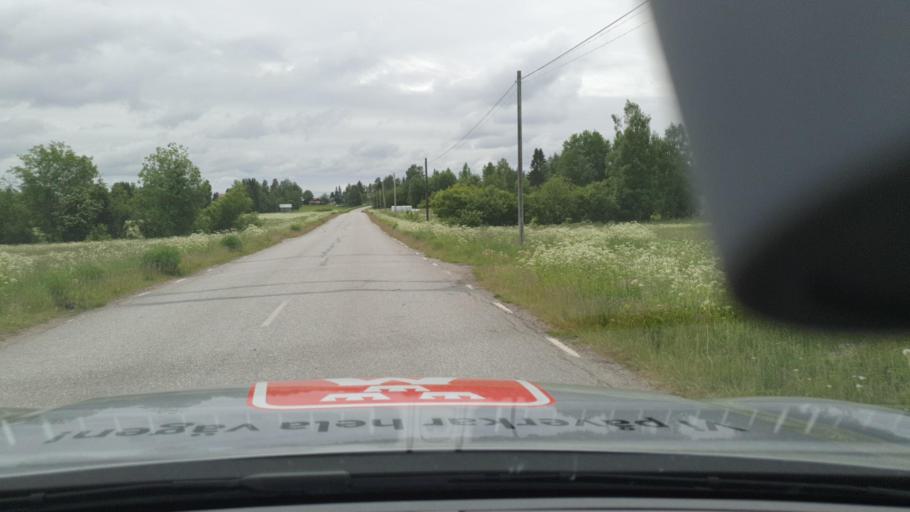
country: SE
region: Norrbotten
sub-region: Lulea Kommun
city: Ranea
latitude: 65.9071
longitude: 22.1769
